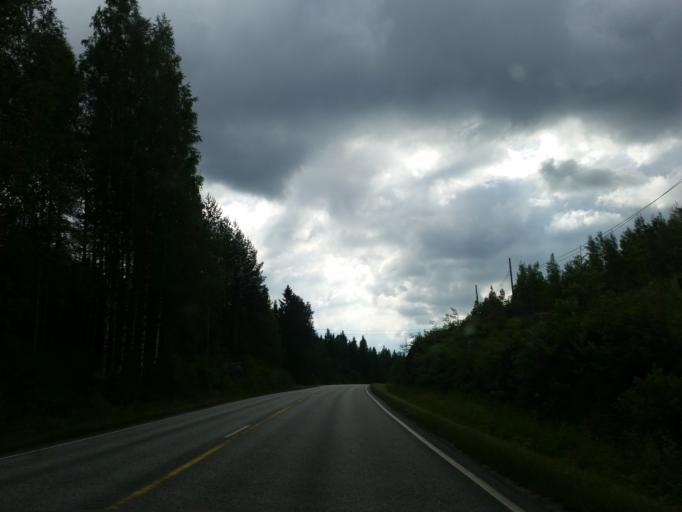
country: FI
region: Northern Savo
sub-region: Sisae-Savo
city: Suonenjoki
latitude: 62.8545
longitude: 27.2662
